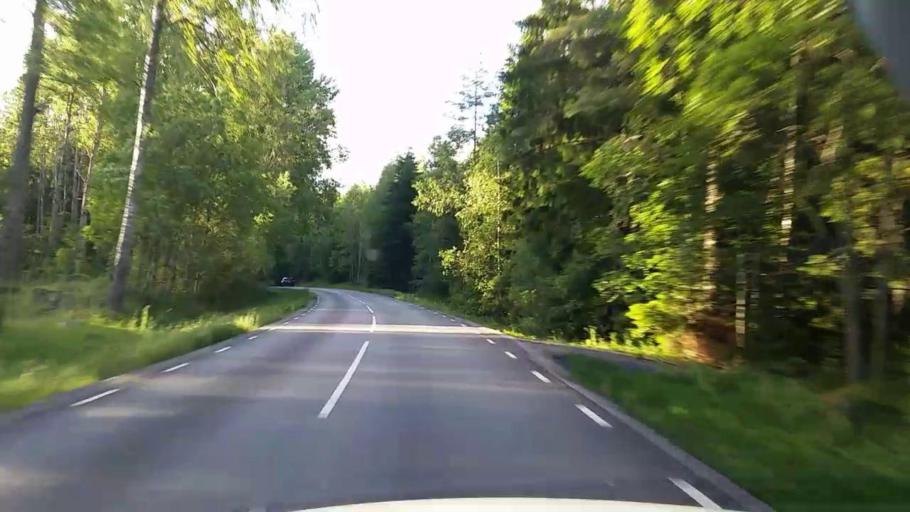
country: SE
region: Vaestmanland
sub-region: Kopings Kommun
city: Kolsva
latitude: 59.6539
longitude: 15.8390
